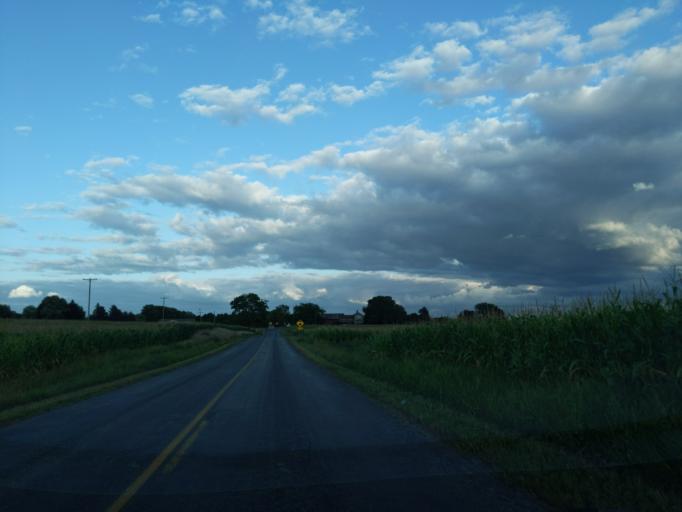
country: US
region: Michigan
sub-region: Ingham County
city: Holt
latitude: 42.5967
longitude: -84.5264
